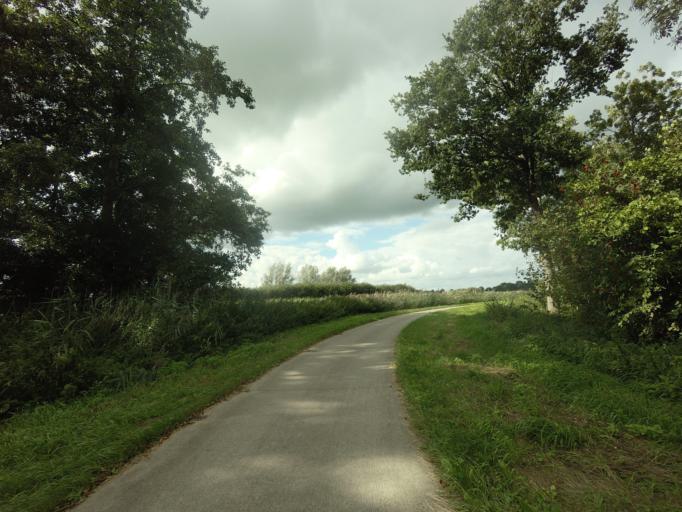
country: NL
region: Overijssel
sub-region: Gemeente Steenwijkerland
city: Blokzijl
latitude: 52.7380
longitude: 6.0007
